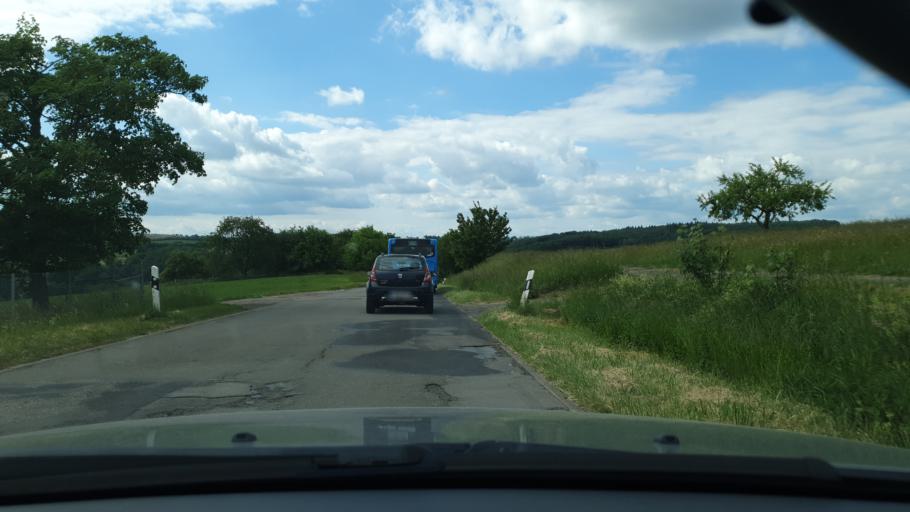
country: DE
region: Rheinland-Pfalz
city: Contwig
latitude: 49.2702
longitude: 7.4285
